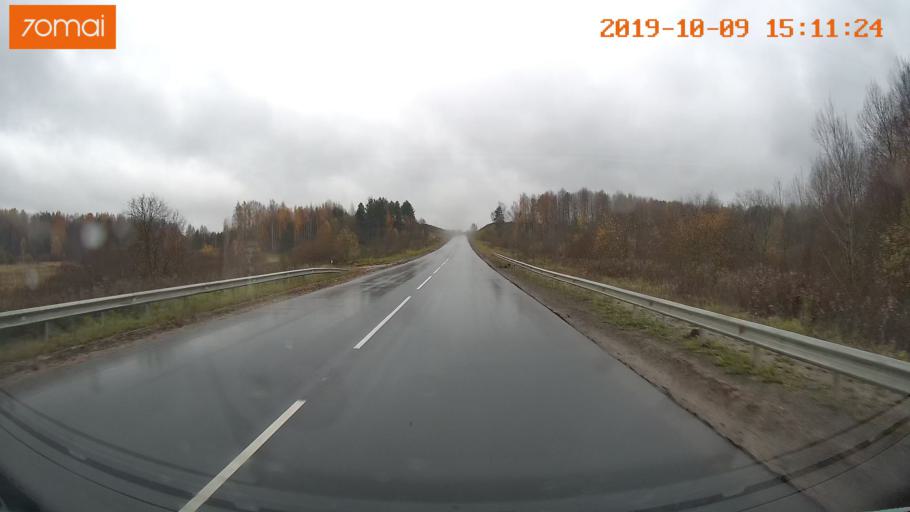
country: RU
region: Kostroma
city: Susanino
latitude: 58.1654
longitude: 41.6301
